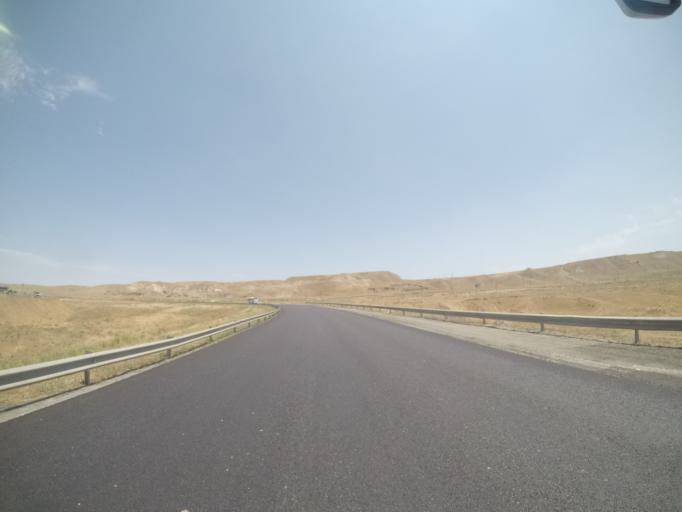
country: AZ
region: Haciqabul
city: Haciqabul
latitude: 40.0160
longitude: 48.9514
